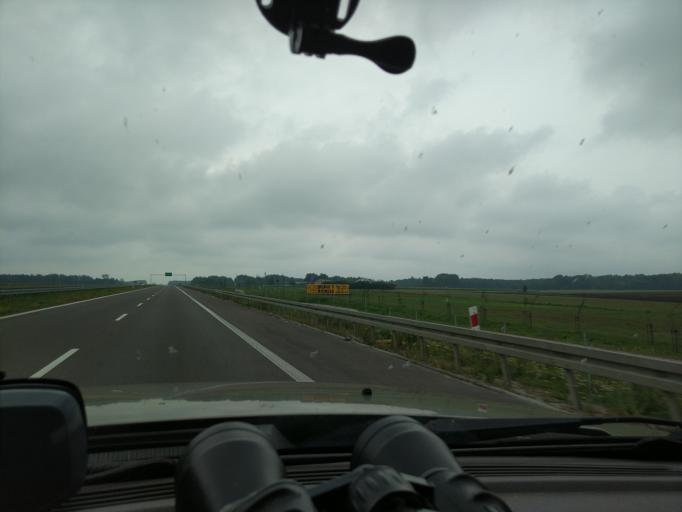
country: PL
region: Podlasie
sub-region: Powiat zambrowski
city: Zambrow
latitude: 53.0291
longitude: 22.3354
